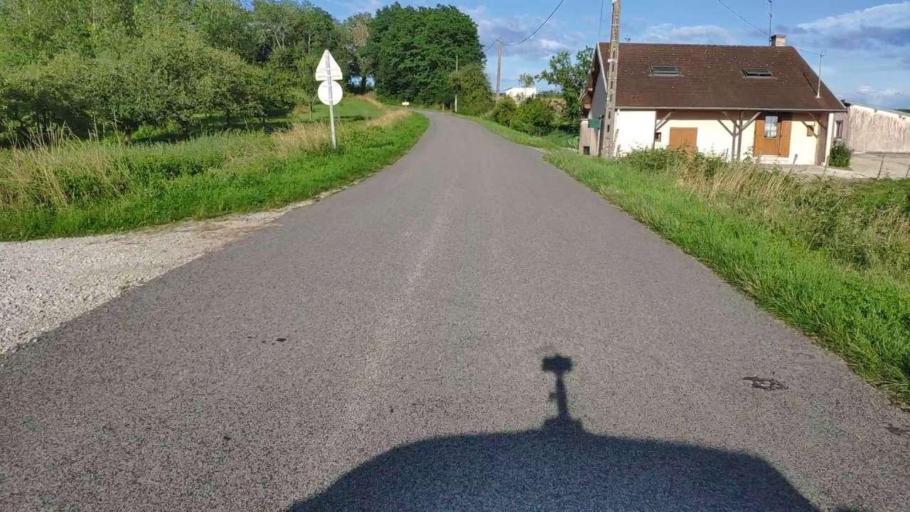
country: FR
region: Franche-Comte
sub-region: Departement du Jura
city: Bletterans
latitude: 46.7823
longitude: 5.4975
